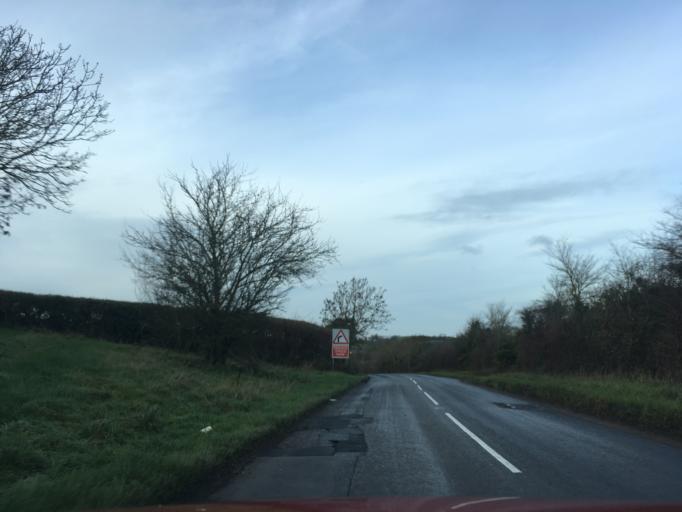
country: GB
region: England
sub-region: South Gloucestershire
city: Almondsbury
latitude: 51.5679
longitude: -2.5656
